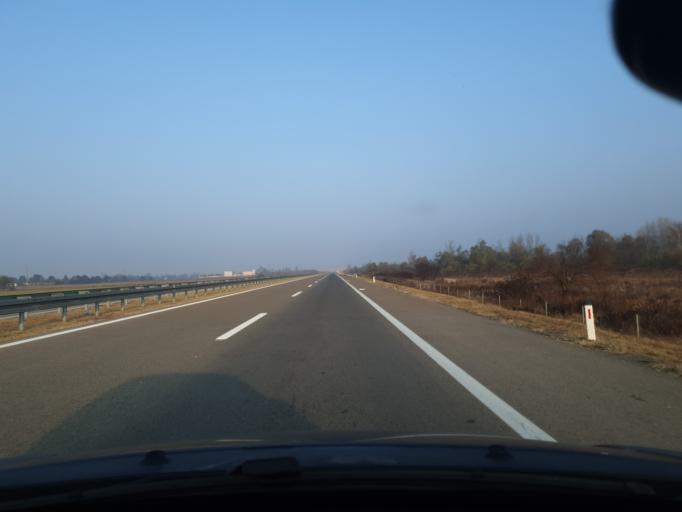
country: RS
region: Central Serbia
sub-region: Jablanicki Okrug
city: Leskovac
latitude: 43.0514
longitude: 21.9815
